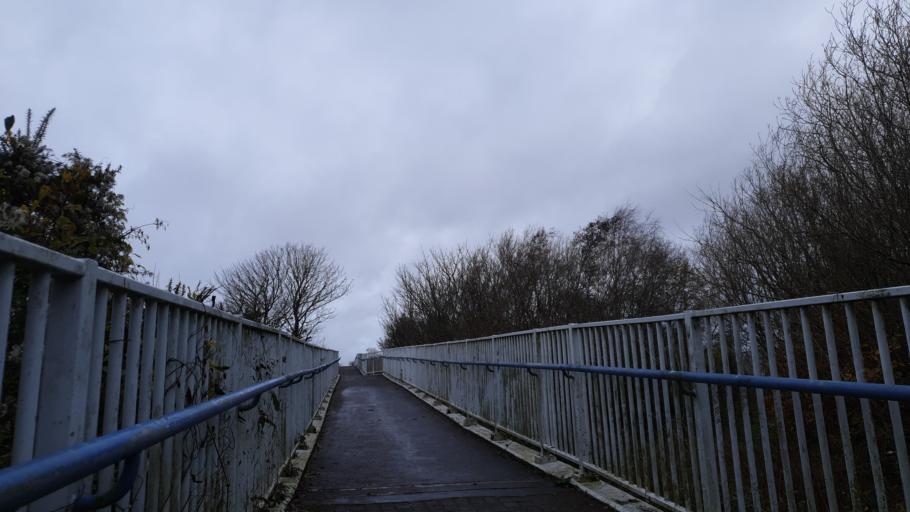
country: IE
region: Munster
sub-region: County Cork
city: Passage West
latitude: 51.8822
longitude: -8.4028
